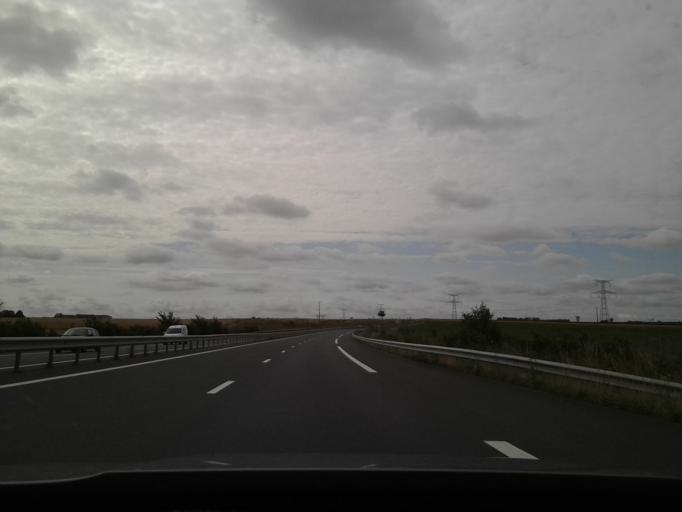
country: FR
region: Lower Normandy
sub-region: Departement du Calvados
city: Ifs
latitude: 49.1268
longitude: -0.3586
